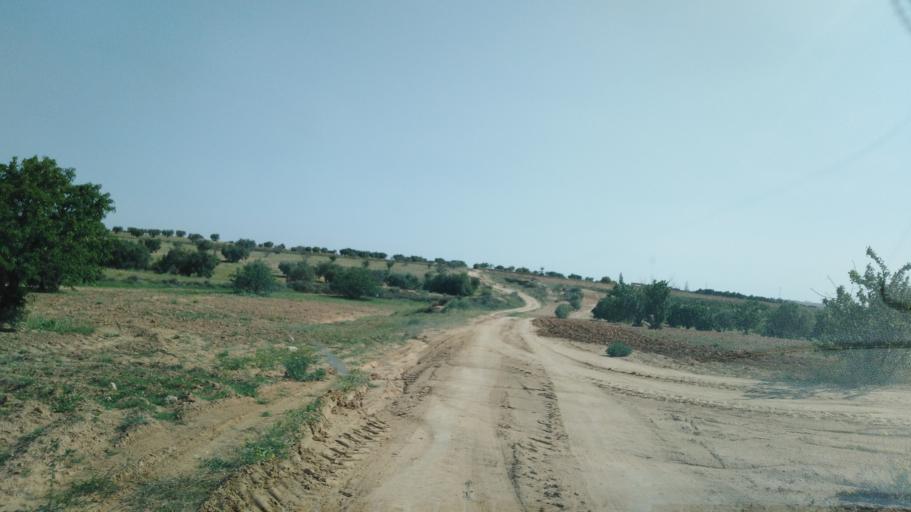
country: TN
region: Safaqis
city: Bi'r `Ali Bin Khalifah
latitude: 34.7888
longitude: 10.3703
